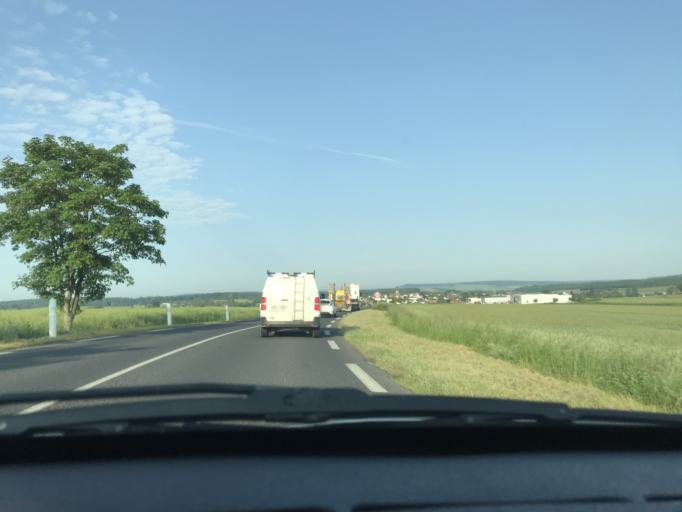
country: FR
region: Lorraine
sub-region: Departement de Meurthe-et-Moselle
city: Champenoux
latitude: 48.7464
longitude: 6.3652
